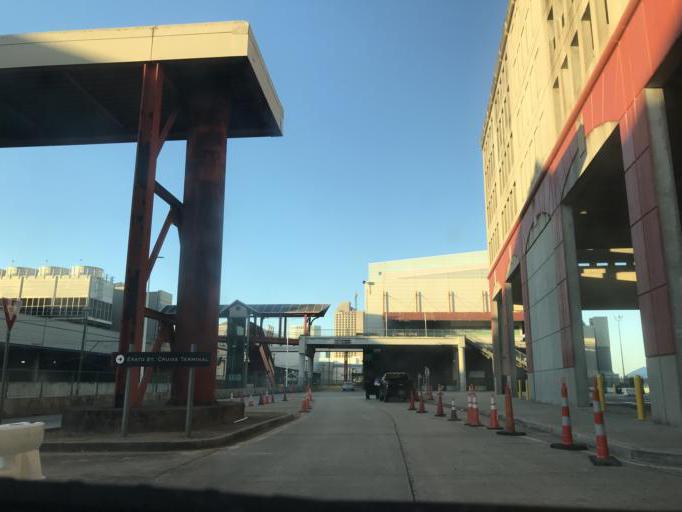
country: US
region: Louisiana
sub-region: Orleans Parish
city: New Orleans
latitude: 29.9404
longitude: -90.0618
